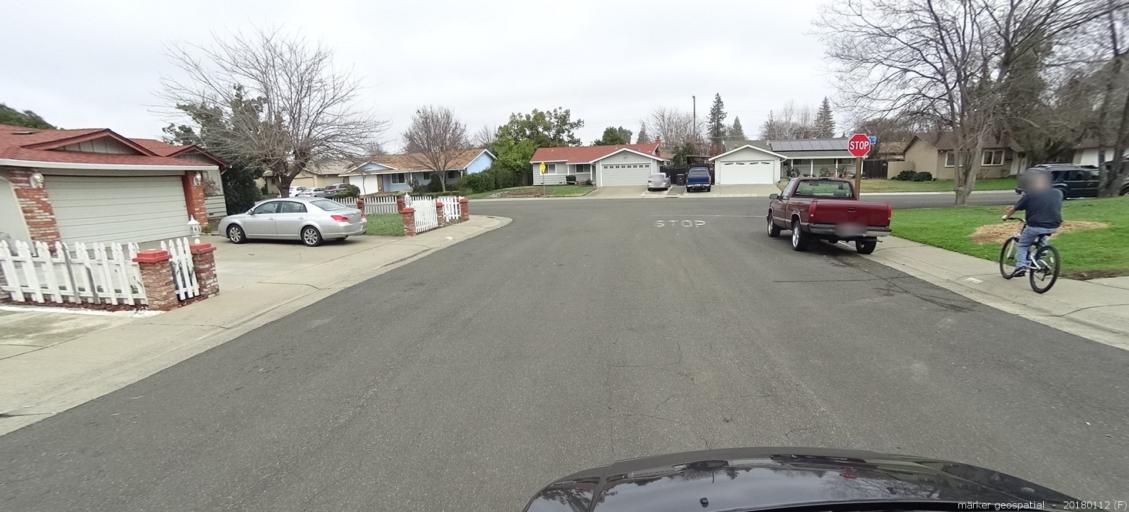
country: US
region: California
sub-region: Sacramento County
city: Rancho Cordova
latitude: 38.6077
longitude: -121.2865
